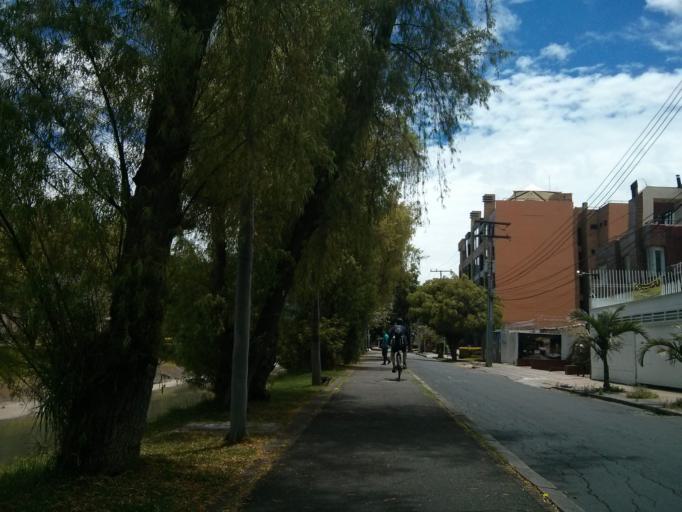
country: CO
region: Bogota D.C.
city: Barrio San Luis
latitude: 4.6960
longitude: -74.0491
